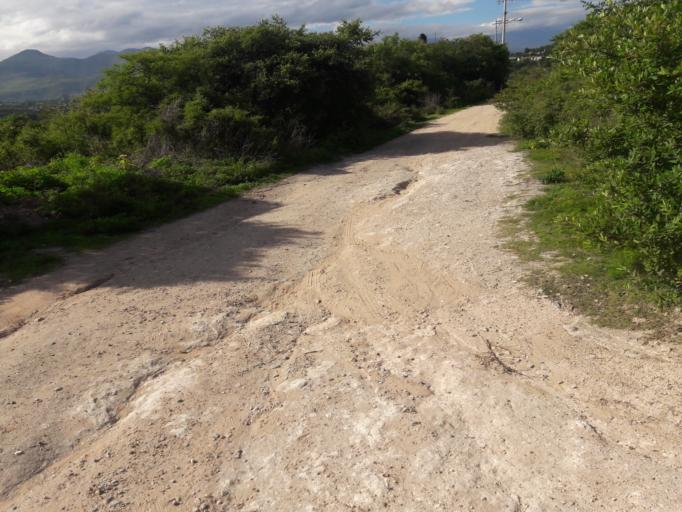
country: MX
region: Oaxaca
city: Ciudad de Huajuapam de Leon
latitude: 17.8409
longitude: -97.7891
